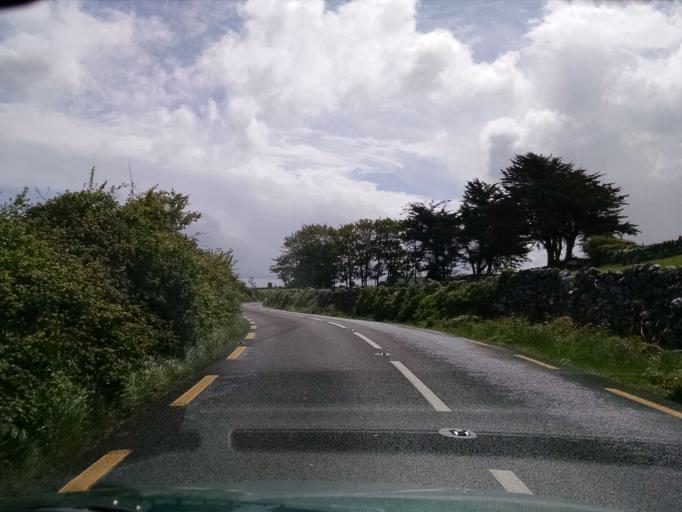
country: IE
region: Connaught
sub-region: County Galway
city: Gaillimh
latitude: 53.1427
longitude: -9.0286
